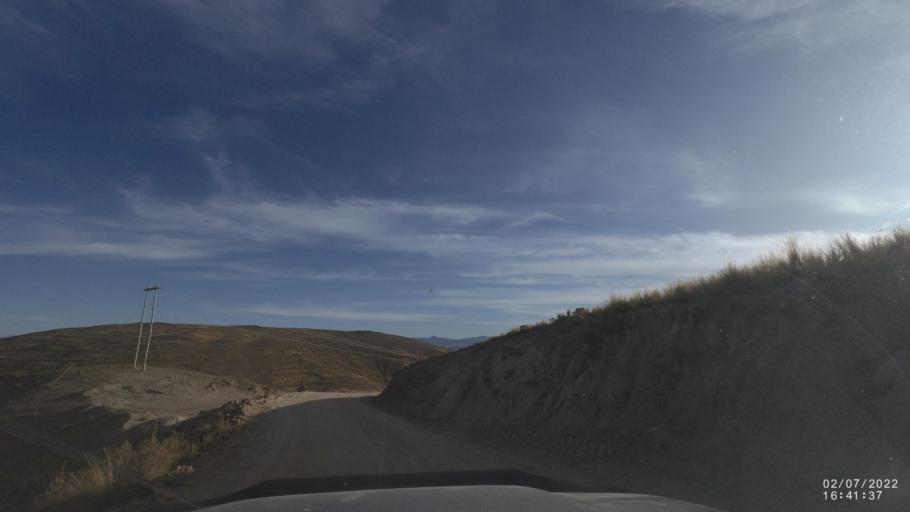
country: BO
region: Cochabamba
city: Irpa Irpa
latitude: -17.9720
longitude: -66.5020
